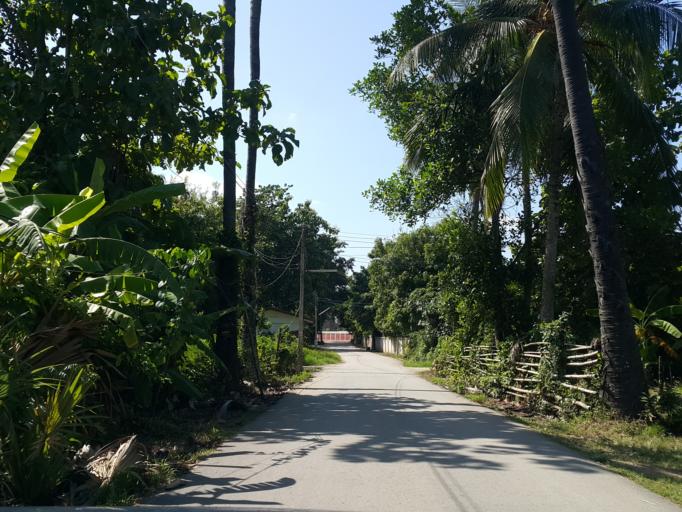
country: TH
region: Chiang Mai
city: San Kamphaeng
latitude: 18.7461
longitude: 99.1712
